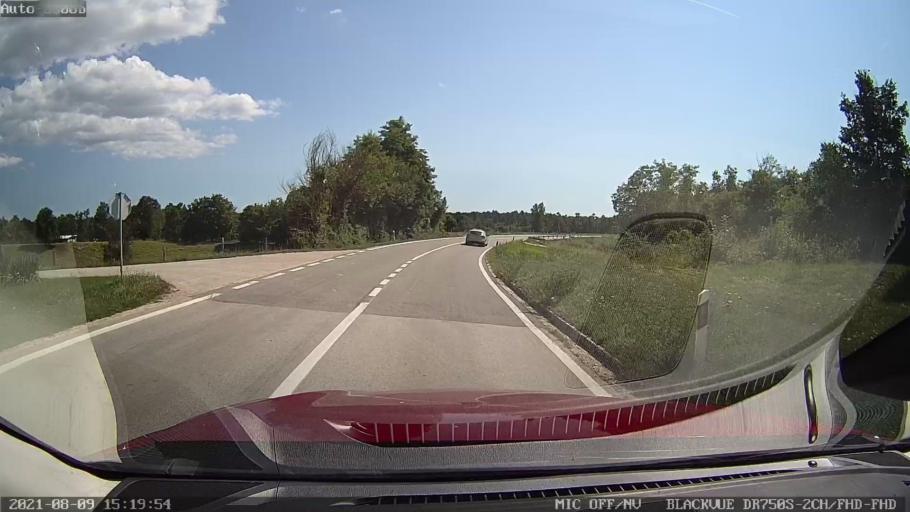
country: HR
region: Istarska
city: Pazin
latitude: 45.2107
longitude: 13.9018
